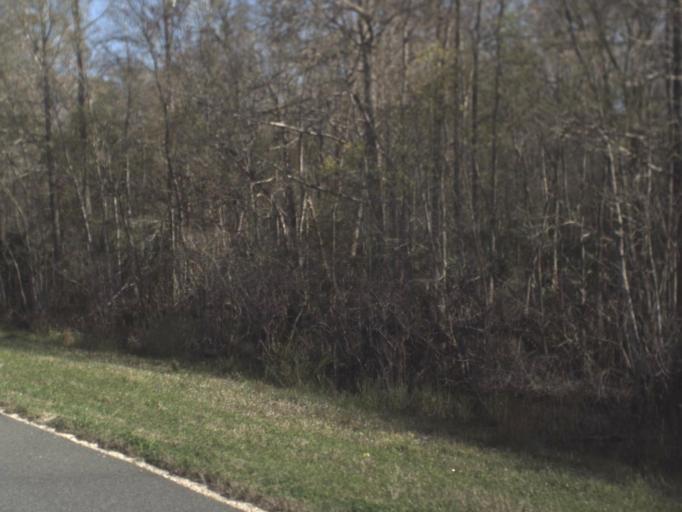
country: US
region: Florida
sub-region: Leon County
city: Woodville
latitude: 30.1728
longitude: -84.0084
